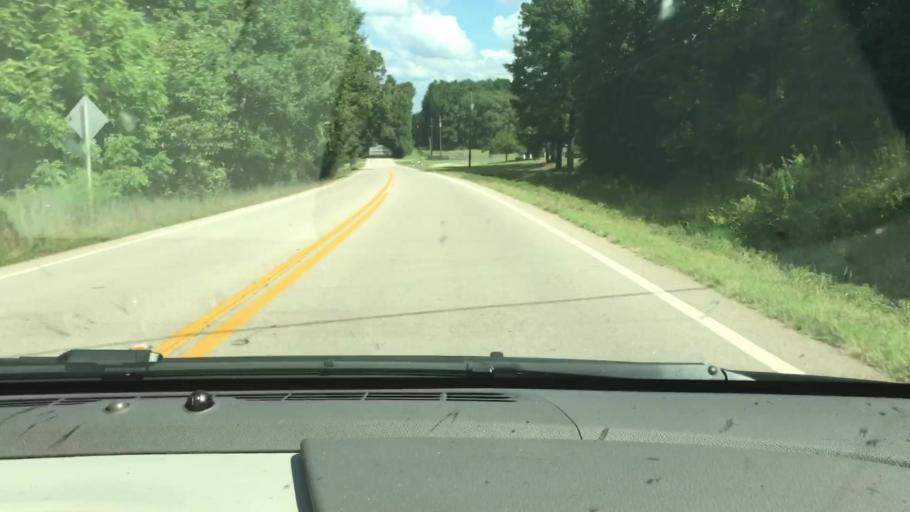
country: US
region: Georgia
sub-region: Troup County
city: La Grange
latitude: 32.9179
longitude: -85.0203
